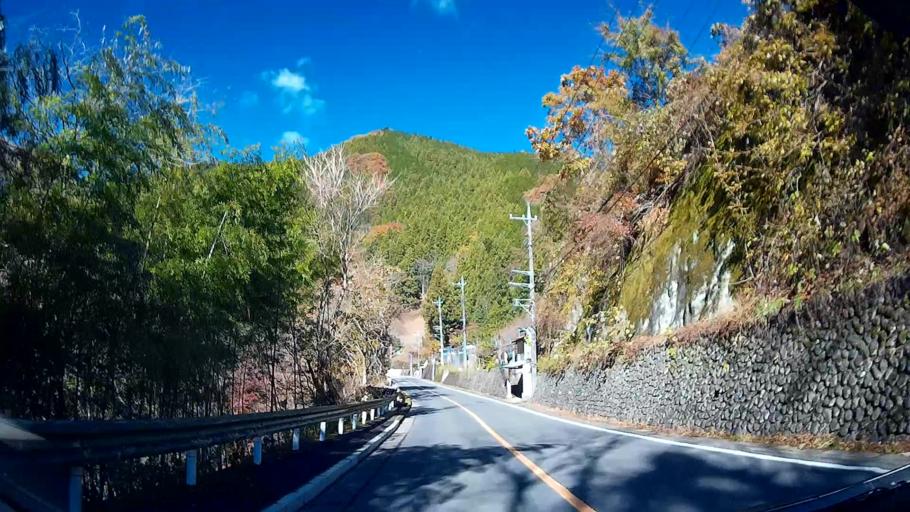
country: JP
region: Tokyo
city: Itsukaichi
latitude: 35.7020
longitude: 139.1382
